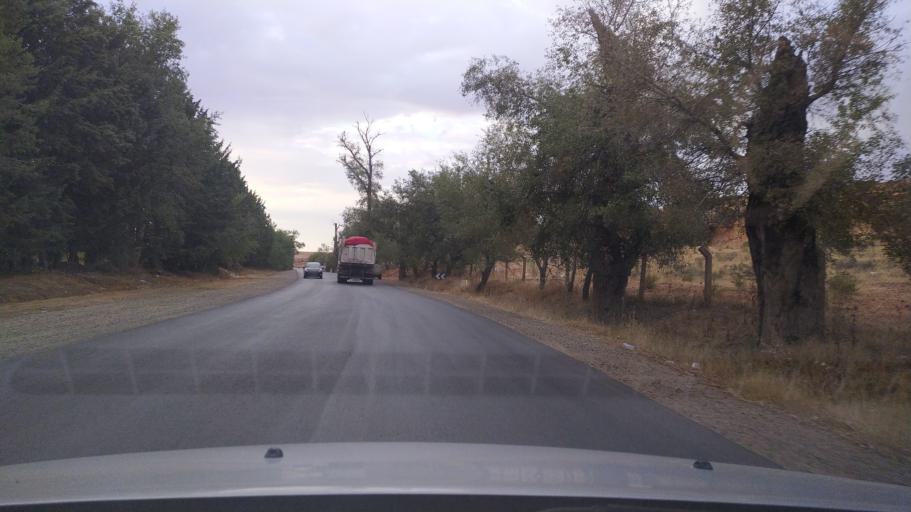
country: DZ
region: Tiaret
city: Frenda
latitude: 35.0483
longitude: 1.0802
